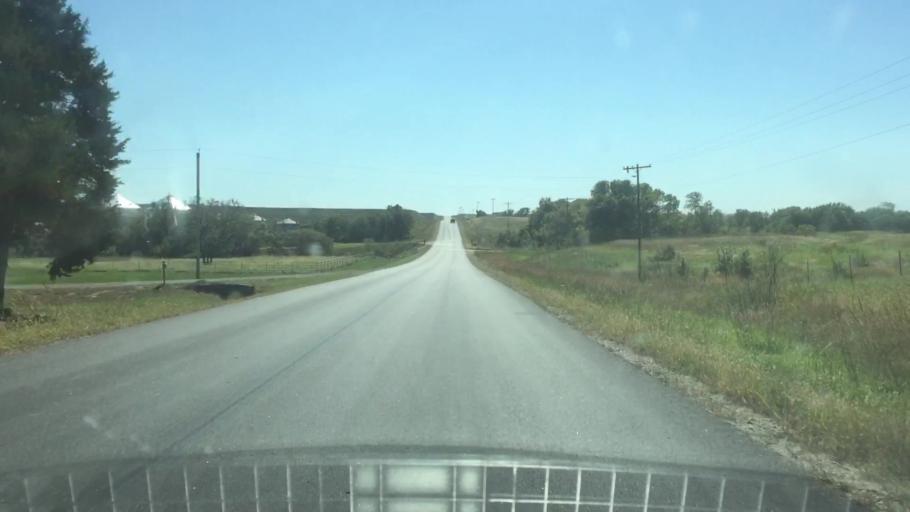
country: US
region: Kansas
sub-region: Marshall County
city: Marysville
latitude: 39.9018
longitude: -96.6010
